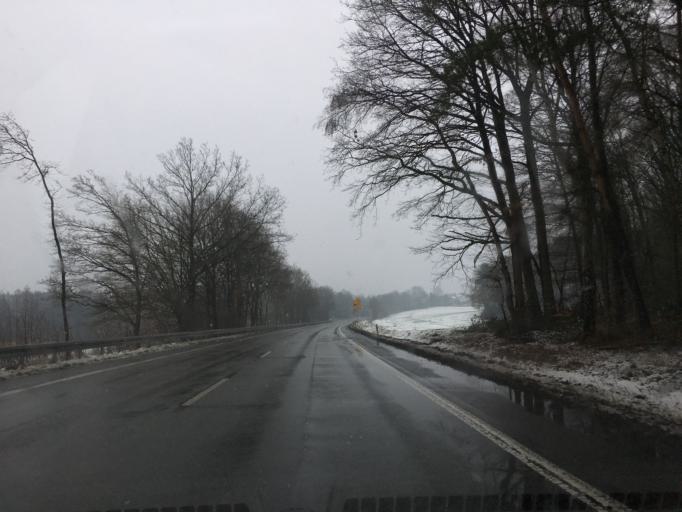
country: DE
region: North Rhine-Westphalia
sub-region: Regierungsbezirk Munster
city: Klein Reken
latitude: 51.8011
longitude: 7.0343
